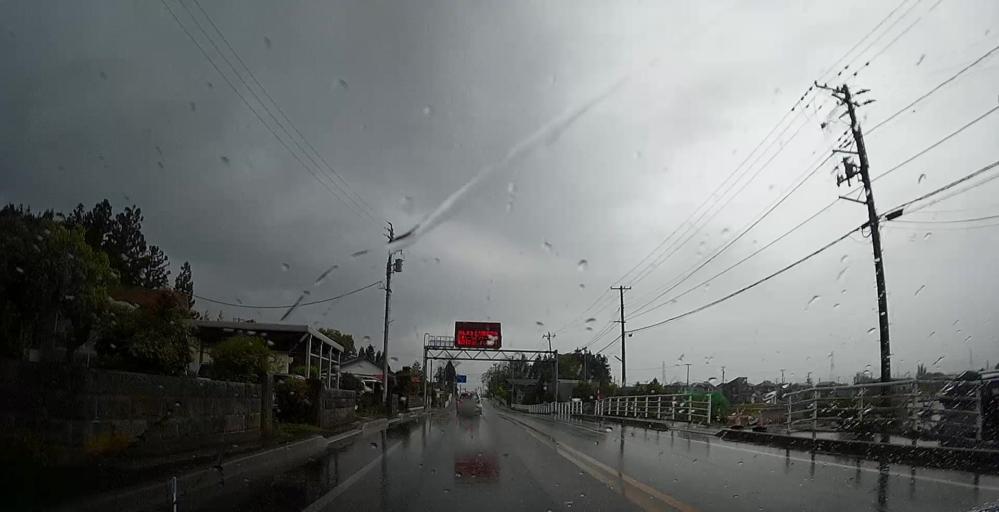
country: JP
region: Niigata
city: Kashiwazaki
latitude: 37.3943
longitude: 138.6023
